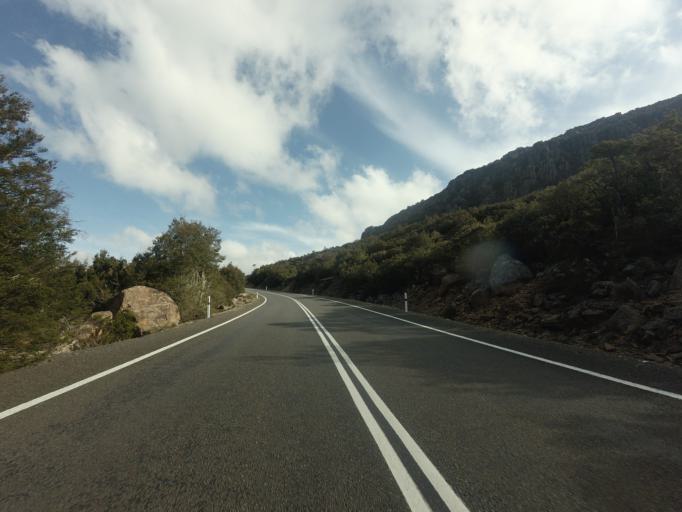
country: AU
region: Tasmania
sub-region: Meander Valley
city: Deloraine
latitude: -41.7278
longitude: 146.7225
